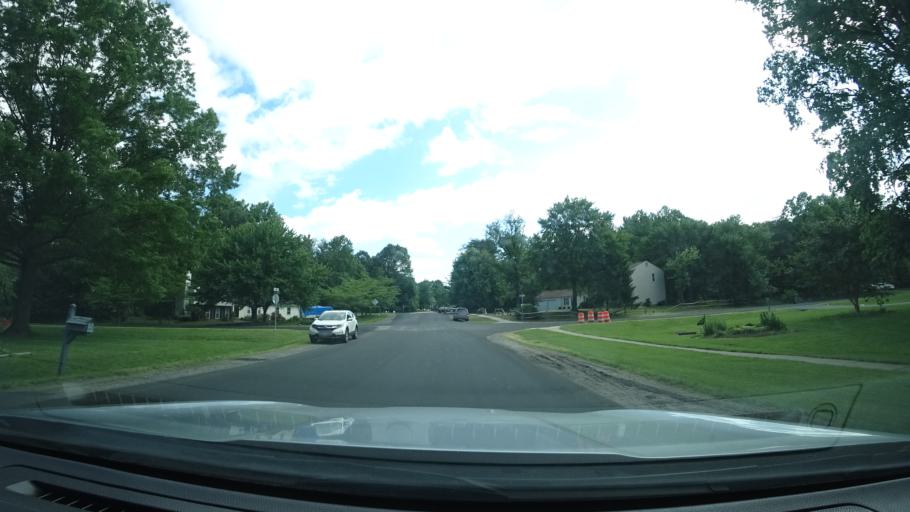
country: US
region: Virginia
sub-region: Fairfax County
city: Herndon
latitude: 38.9414
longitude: -77.3729
